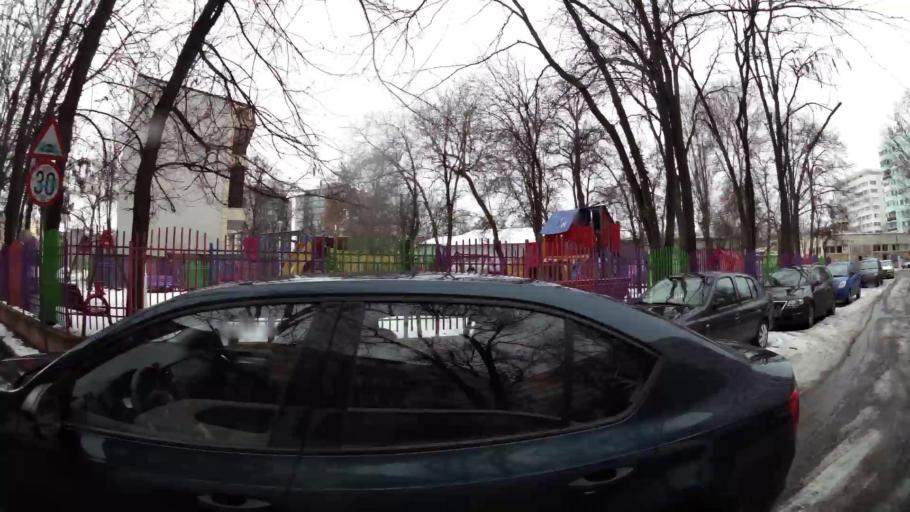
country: RO
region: Ilfov
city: Dobroesti
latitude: 44.4251
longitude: 26.1736
